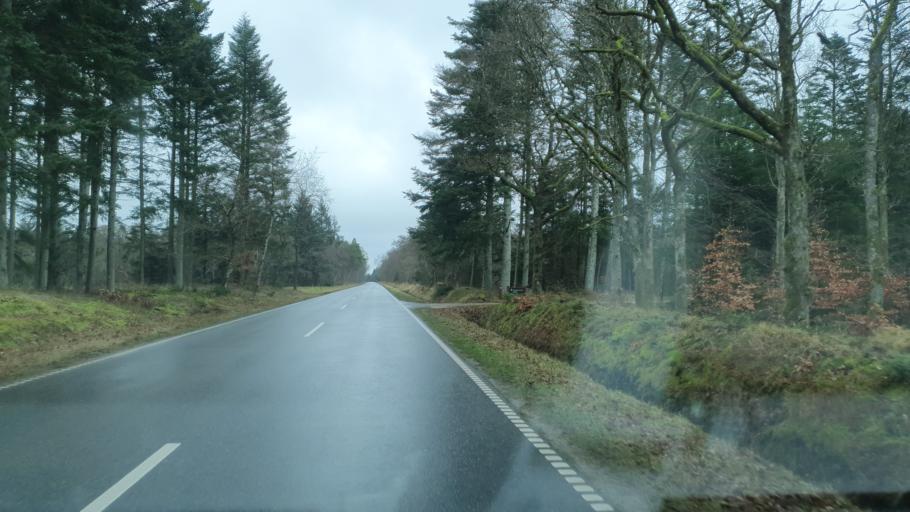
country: DK
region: North Denmark
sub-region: Jammerbugt Kommune
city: Fjerritslev
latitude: 57.1228
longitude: 9.1281
